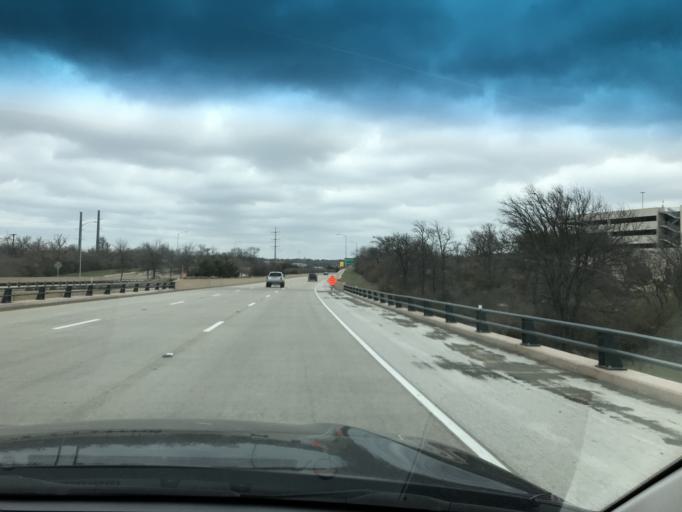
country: US
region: Texas
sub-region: Tarrant County
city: Westworth
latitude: 32.7073
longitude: -97.4046
